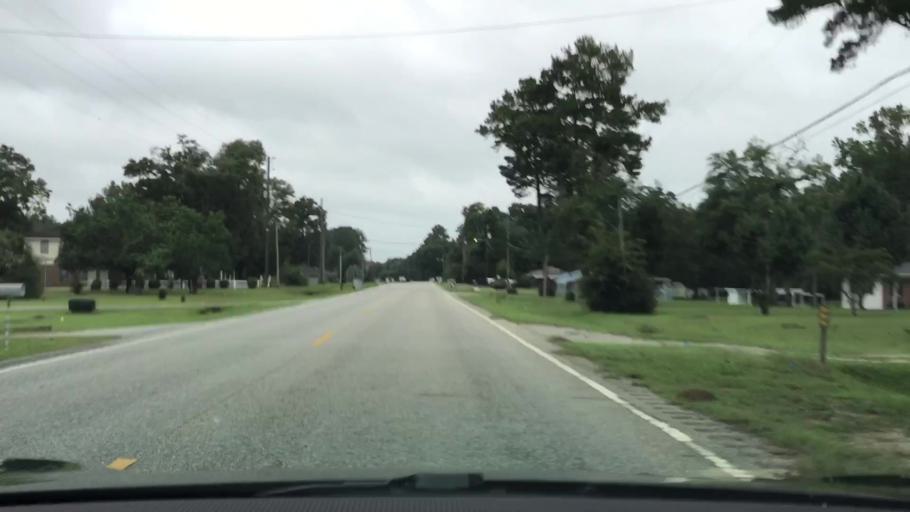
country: US
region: Alabama
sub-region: Coffee County
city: Elba
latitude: 31.3876
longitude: -86.0852
